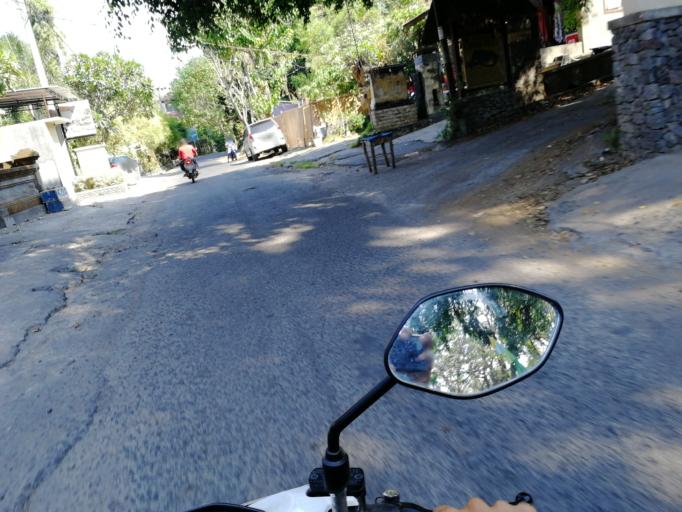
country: ID
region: Bali
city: Biaslantang Kaler
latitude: -8.3429
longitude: 115.6686
